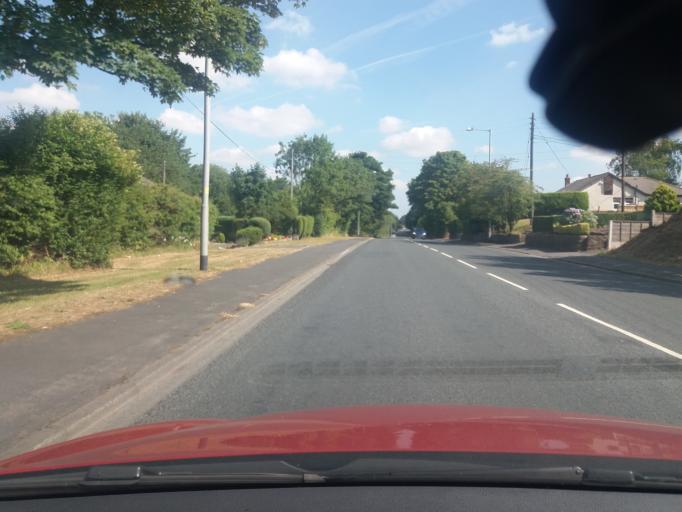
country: GB
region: England
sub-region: Lancashire
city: Adlington
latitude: 53.6234
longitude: -2.6114
